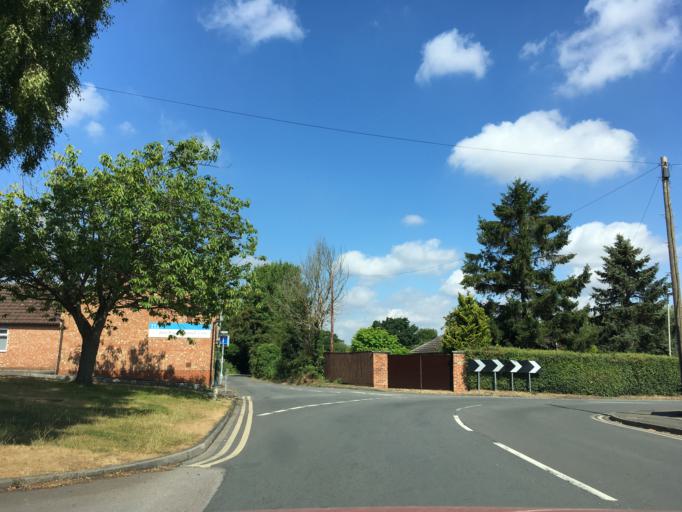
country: GB
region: England
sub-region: Gloucestershire
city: Uckington
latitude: 51.8970
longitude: -2.1313
